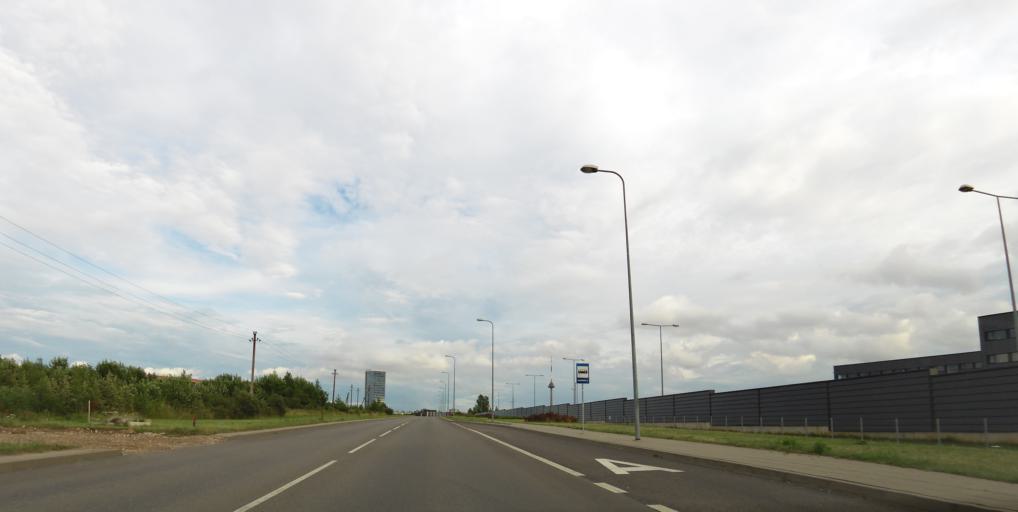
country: LT
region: Vilnius County
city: Justiniskes
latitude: 54.7083
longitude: 25.2033
